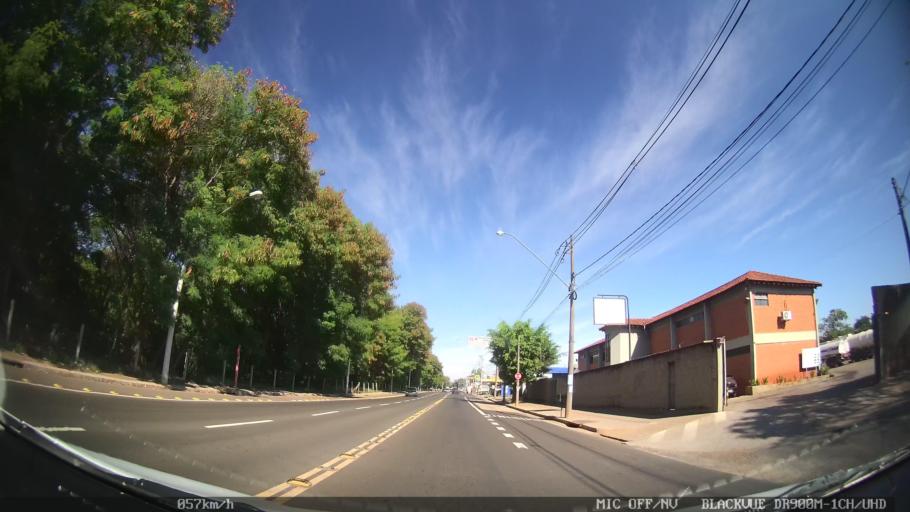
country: BR
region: Sao Paulo
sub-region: Sao Jose Do Rio Preto
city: Sao Jose do Rio Preto
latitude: -20.7910
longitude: -49.3919
